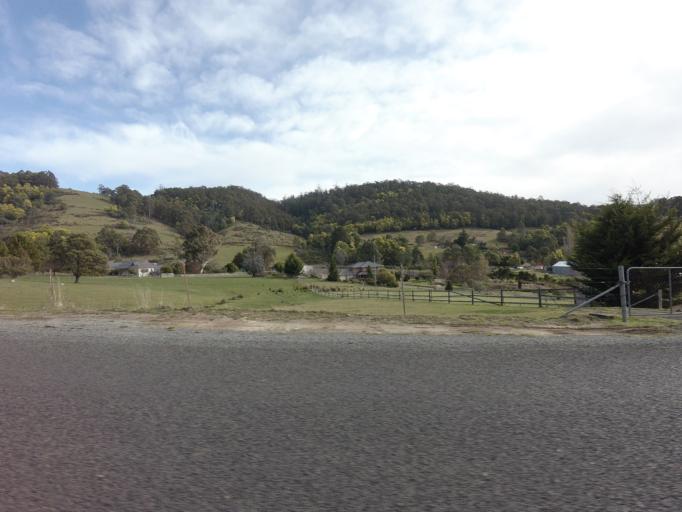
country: AU
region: Tasmania
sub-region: Kingborough
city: Margate
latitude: -42.9933
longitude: 147.1848
